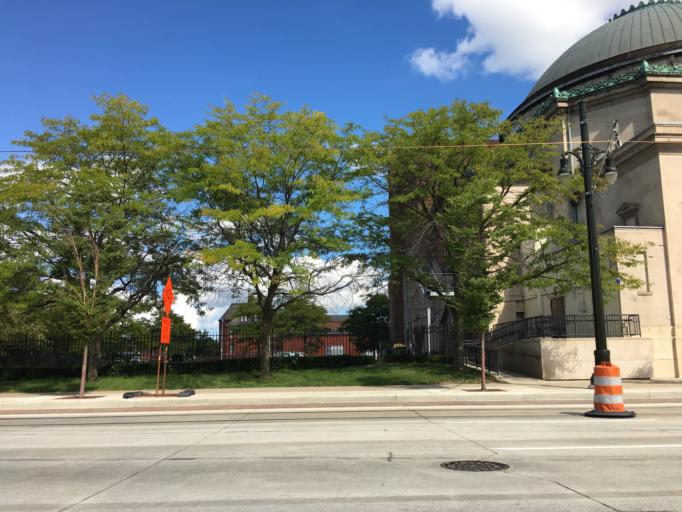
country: US
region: Michigan
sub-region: Wayne County
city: Detroit
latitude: 42.3463
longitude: -83.0572
